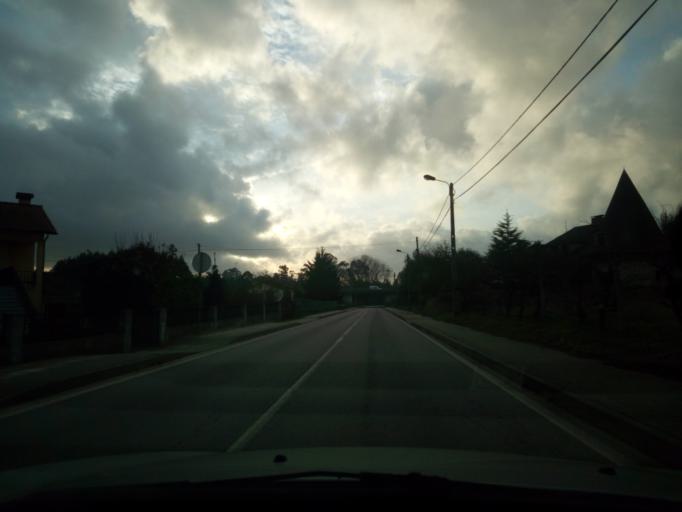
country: PT
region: Aveiro
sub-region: Agueda
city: Agueda
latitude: 40.5577
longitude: -8.4732
